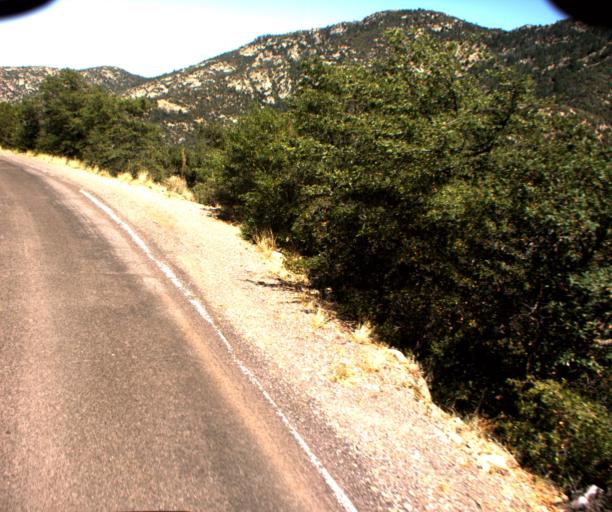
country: US
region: Arizona
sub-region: Graham County
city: Swift Trail Junction
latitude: 32.6493
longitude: -109.8094
